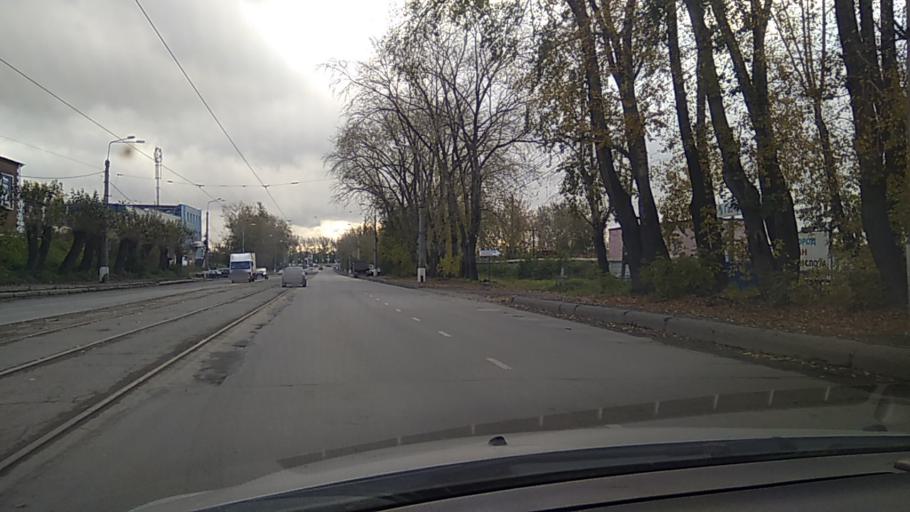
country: RU
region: Sverdlovsk
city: Nizhniy Tagil
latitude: 57.9255
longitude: 59.9912
